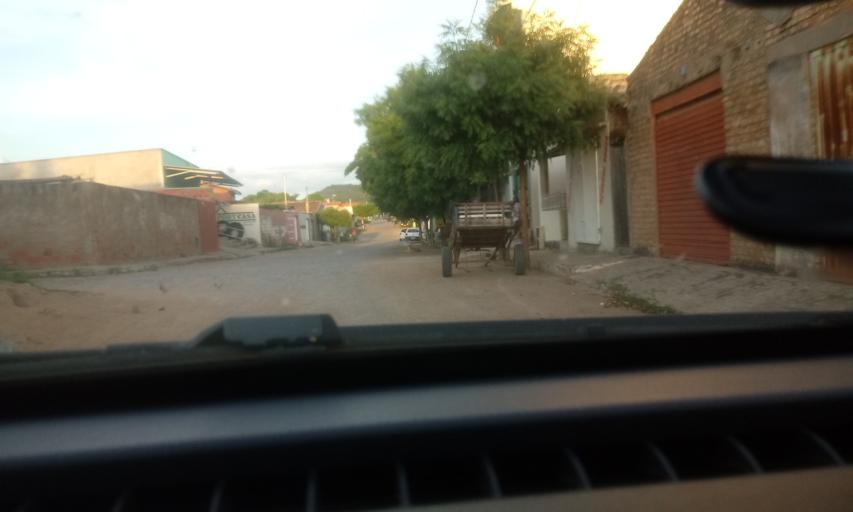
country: BR
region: Bahia
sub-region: Riacho De Santana
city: Riacho de Santana
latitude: -13.9117
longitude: -42.8461
